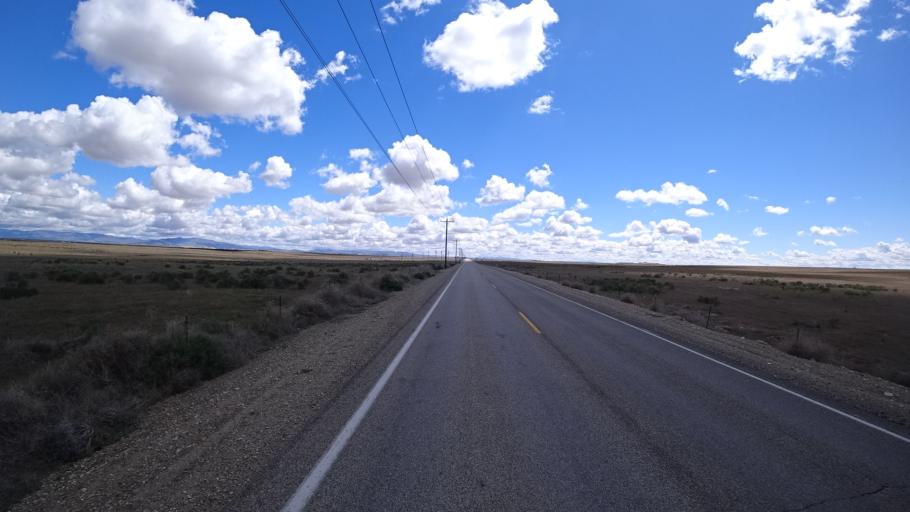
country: US
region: Idaho
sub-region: Ada County
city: Kuna
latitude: 43.4592
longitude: -116.2993
